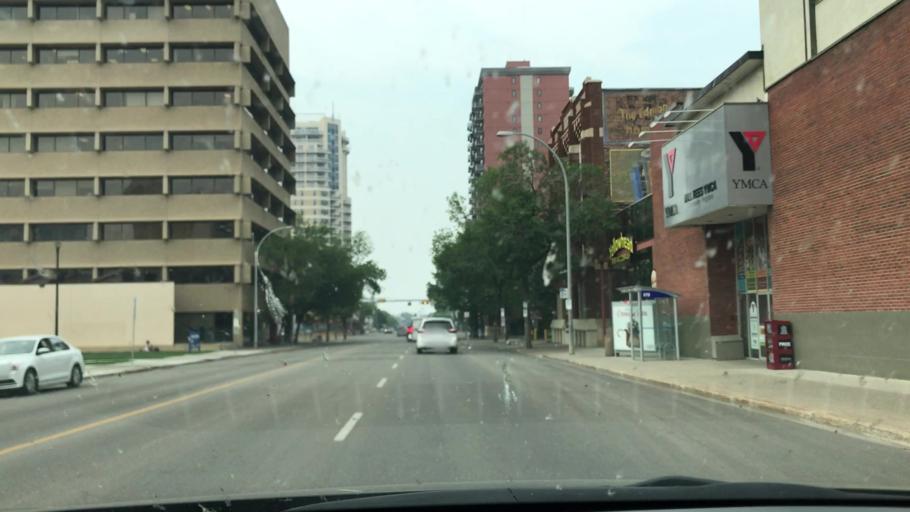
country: CA
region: Alberta
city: Edmonton
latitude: 53.5432
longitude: -113.5011
